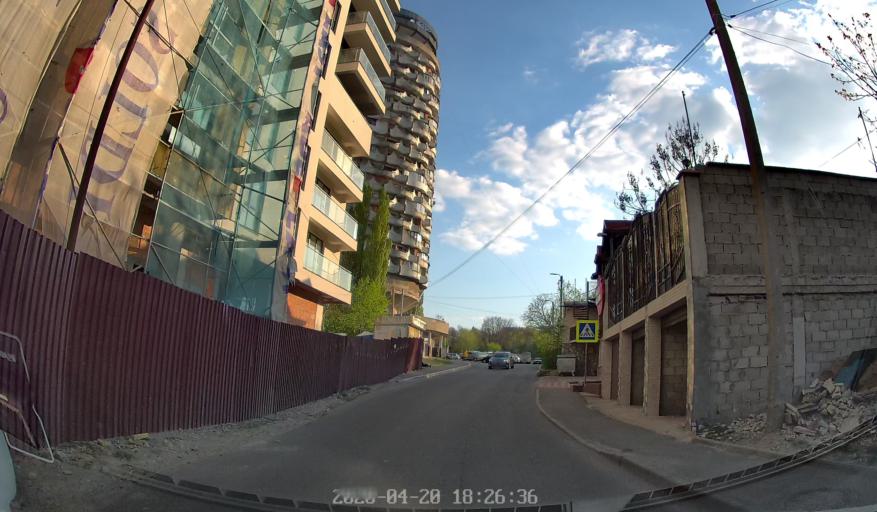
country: MD
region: Chisinau
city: Chisinau
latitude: 46.9916
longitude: 28.8378
